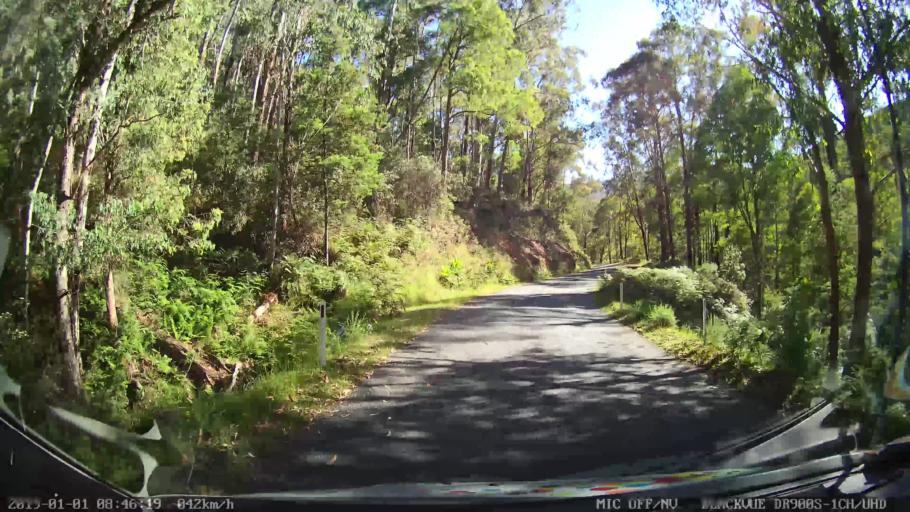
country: AU
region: New South Wales
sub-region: Snowy River
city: Jindabyne
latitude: -36.3008
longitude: 148.1927
